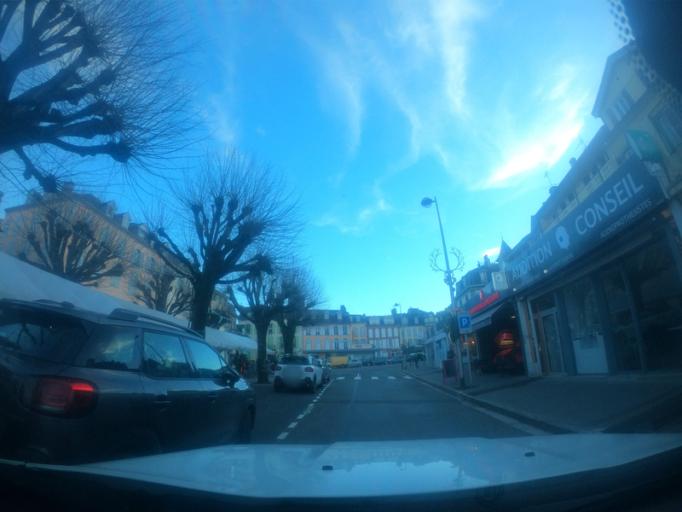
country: FR
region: Midi-Pyrenees
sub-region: Departement des Hautes-Pyrenees
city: Bagneres-de-Bigorre
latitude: 43.0639
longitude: 0.1501
